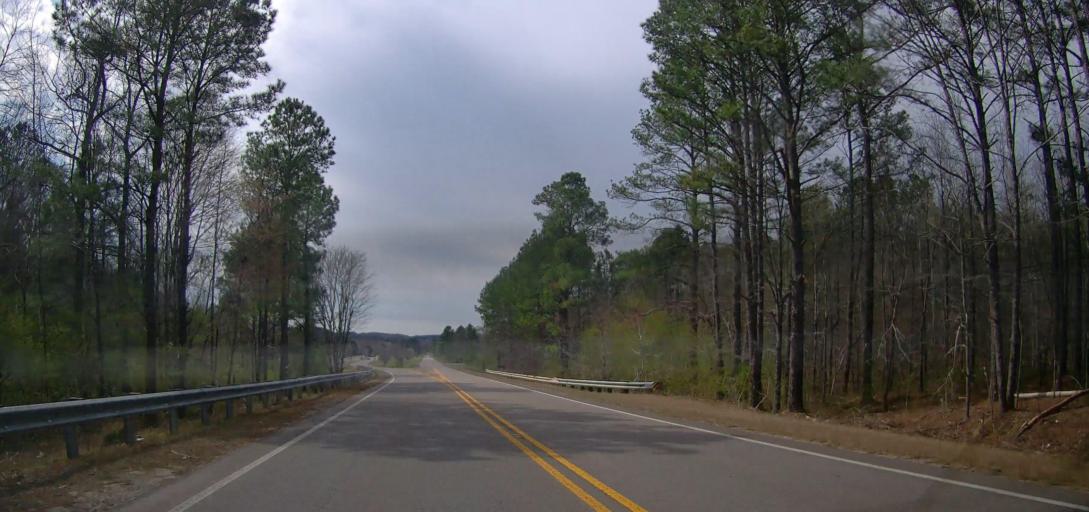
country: US
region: Alabama
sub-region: Walker County
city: Carbon Hill
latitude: 33.8768
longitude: -87.4907
